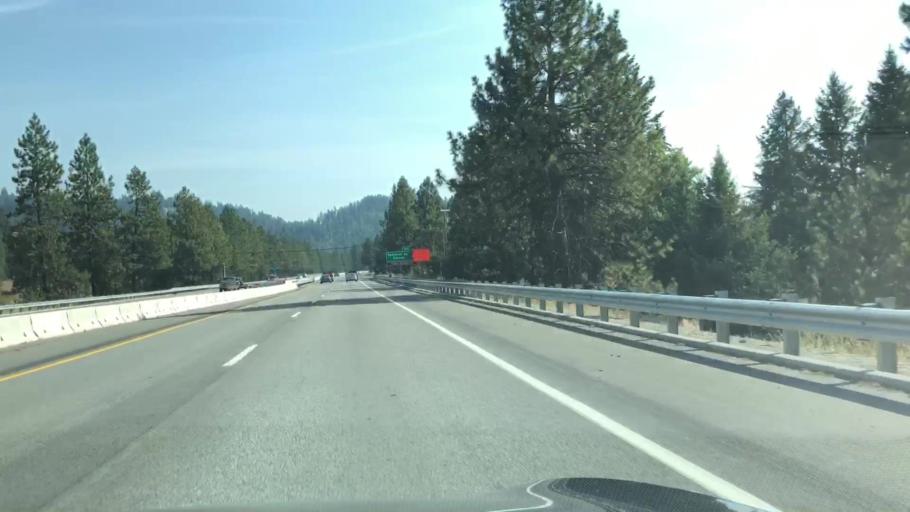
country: US
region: Idaho
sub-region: Kootenai County
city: Coeur d'Alene
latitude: 47.6801
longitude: -116.7566
